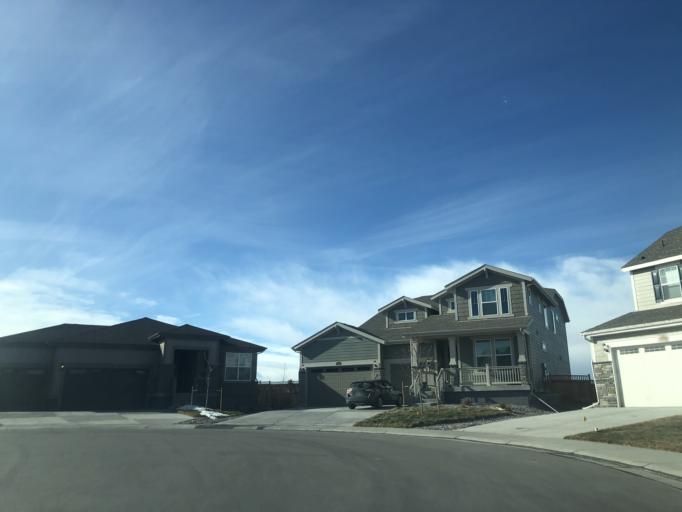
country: US
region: Colorado
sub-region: Douglas County
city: Stonegate
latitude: 39.5569
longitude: -104.8059
